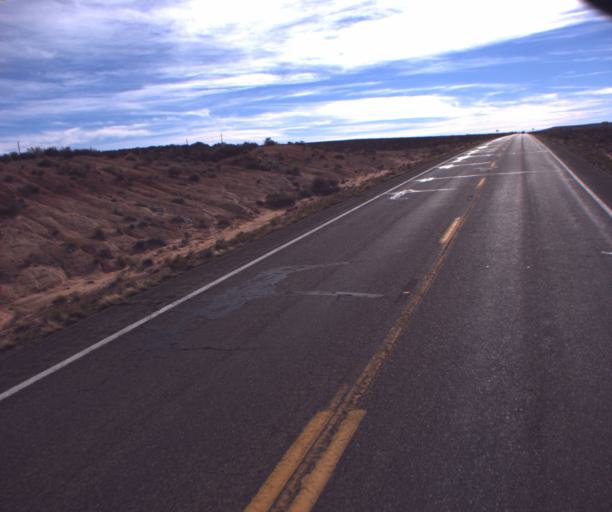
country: US
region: Arizona
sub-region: Coconino County
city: LeChee
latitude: 36.8317
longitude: -111.3146
